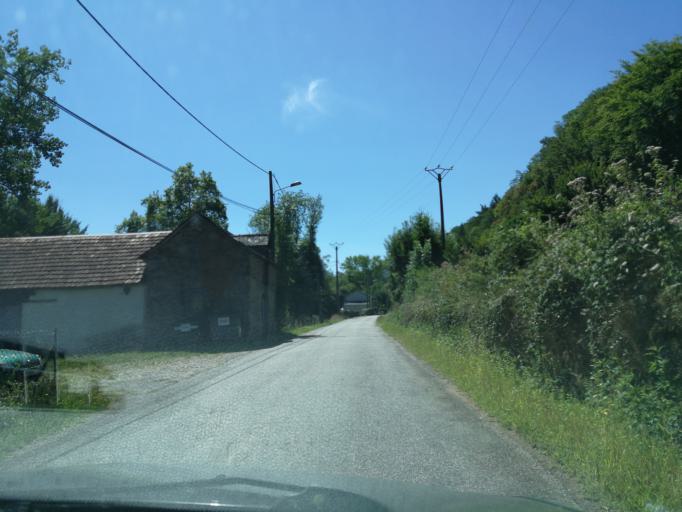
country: FR
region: Limousin
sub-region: Departement de la Correze
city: Argentat
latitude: 45.0907
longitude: 1.9260
